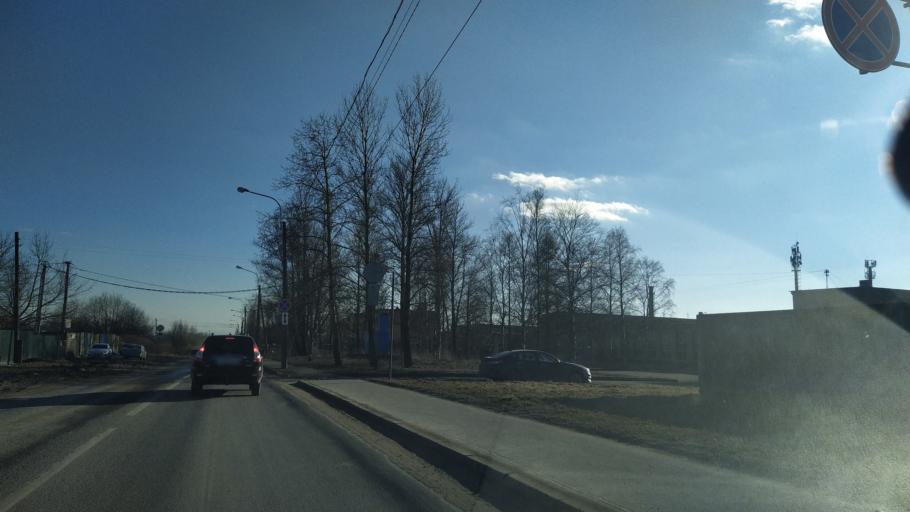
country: RU
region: St.-Petersburg
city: Pushkin
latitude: 59.6988
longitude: 30.3947
